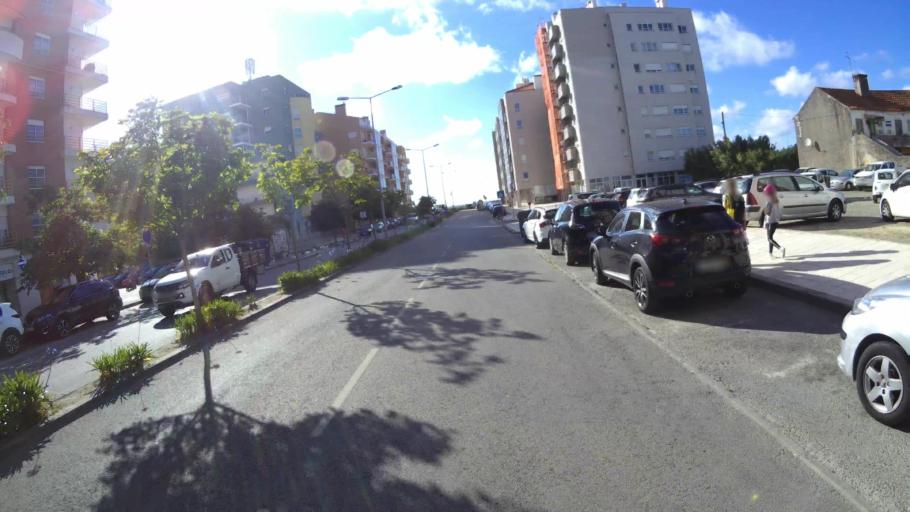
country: PT
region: Aveiro
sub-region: Aveiro
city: Aveiro
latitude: 40.6481
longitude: -8.6455
